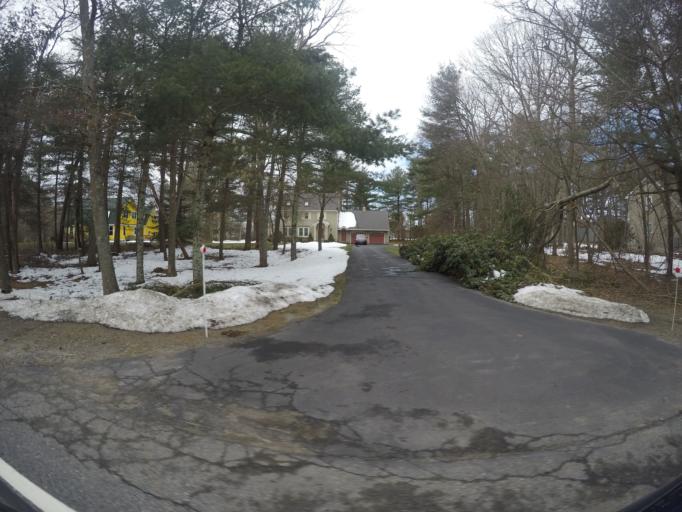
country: US
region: Massachusetts
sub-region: Bristol County
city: Easton
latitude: 42.0552
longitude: -71.1306
